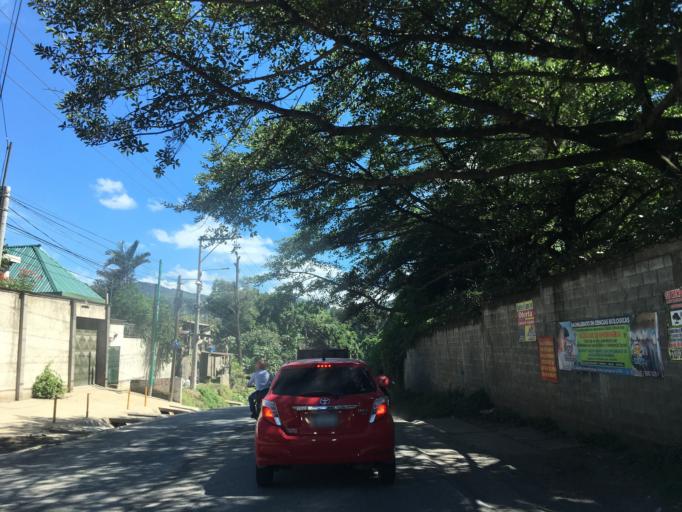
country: GT
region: Guatemala
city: Villa Nueva
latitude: 14.5333
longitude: -90.6166
